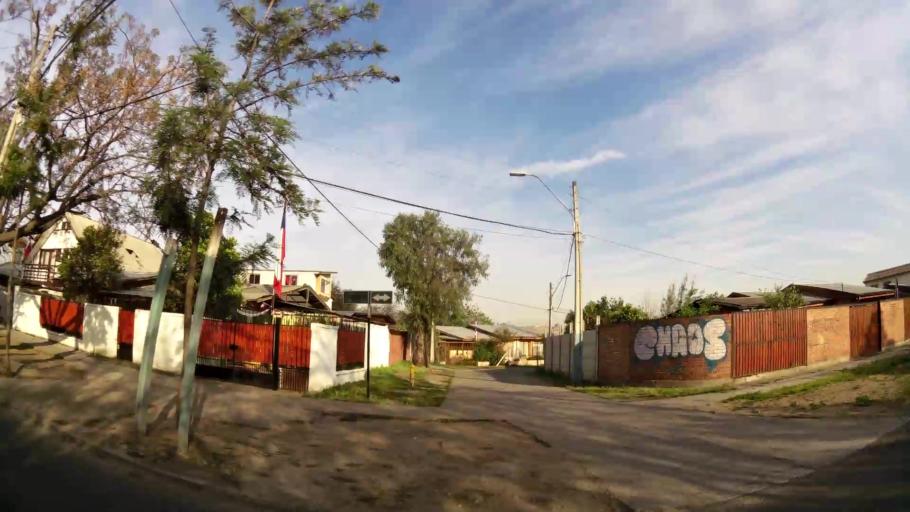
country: CL
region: Santiago Metropolitan
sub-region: Provincia de Santiago
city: La Pintana
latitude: -33.5293
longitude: -70.6708
